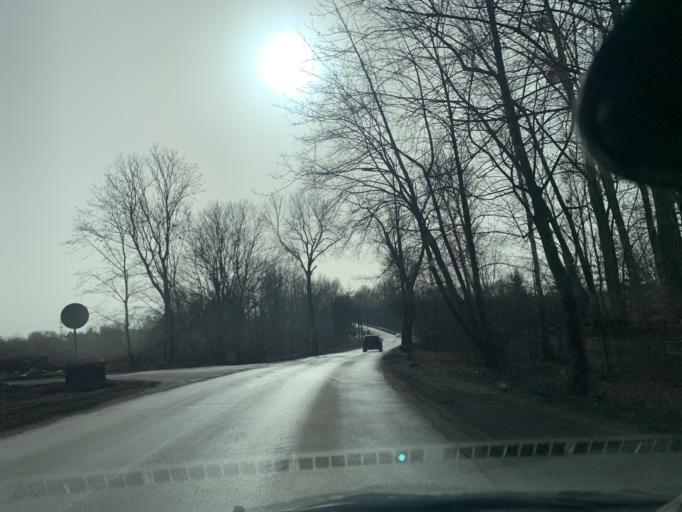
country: PL
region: Silesian Voivodeship
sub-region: Swietochlowice
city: Swietochlowice
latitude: 50.3290
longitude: 18.8945
